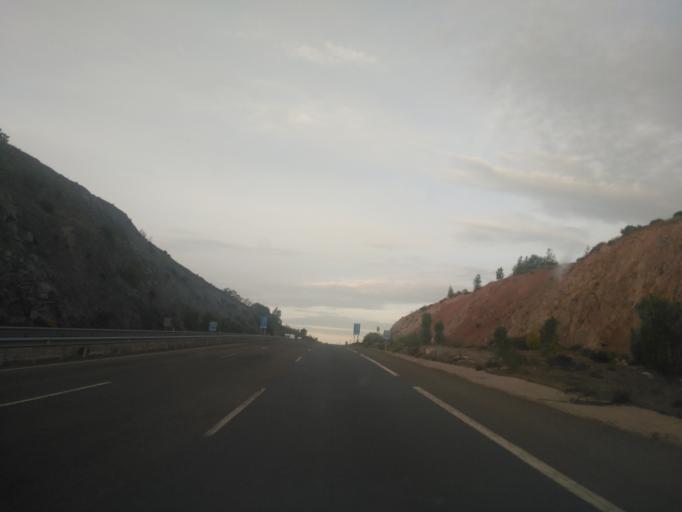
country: ES
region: Castille and Leon
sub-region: Provincia de Salamanca
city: Fresnedoso
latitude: 40.4236
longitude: -5.7058
